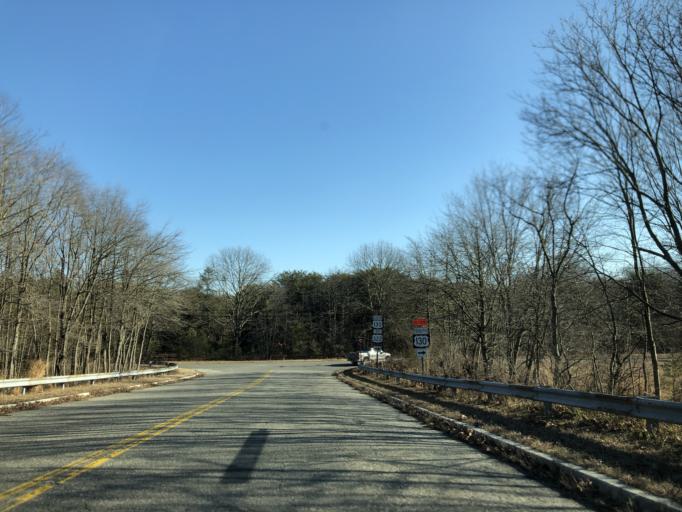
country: US
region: Pennsylvania
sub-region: Delaware County
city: Chester
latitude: 39.8046
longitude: -75.3413
